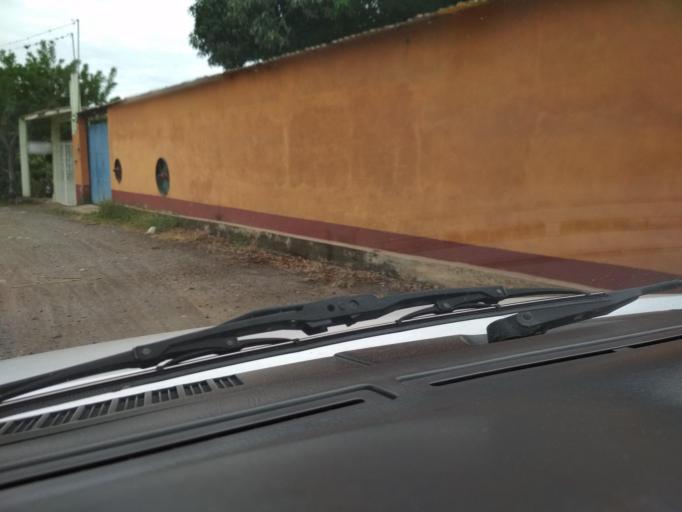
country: MX
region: Veracruz
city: Alto Lucero
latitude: 19.5947
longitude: -96.7838
